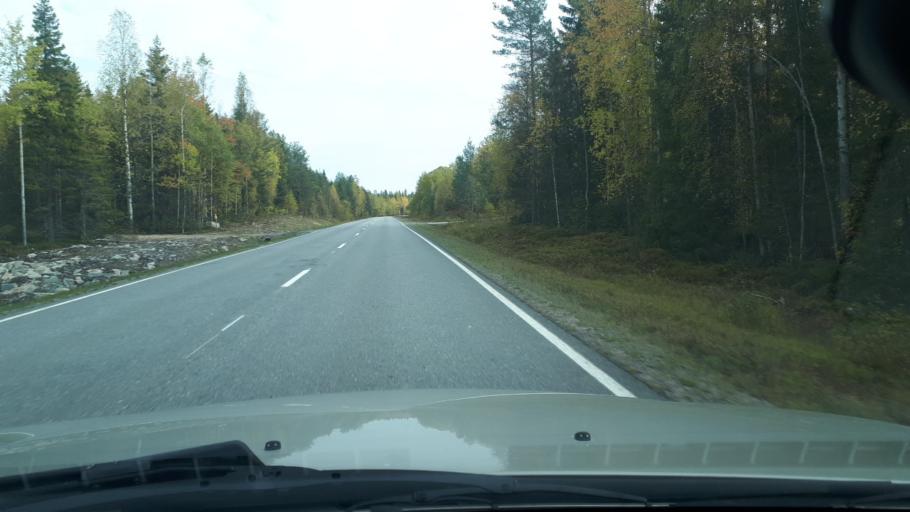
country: FI
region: Lapland
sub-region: Rovaniemi
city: Ranua
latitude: 66.0070
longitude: 26.2738
